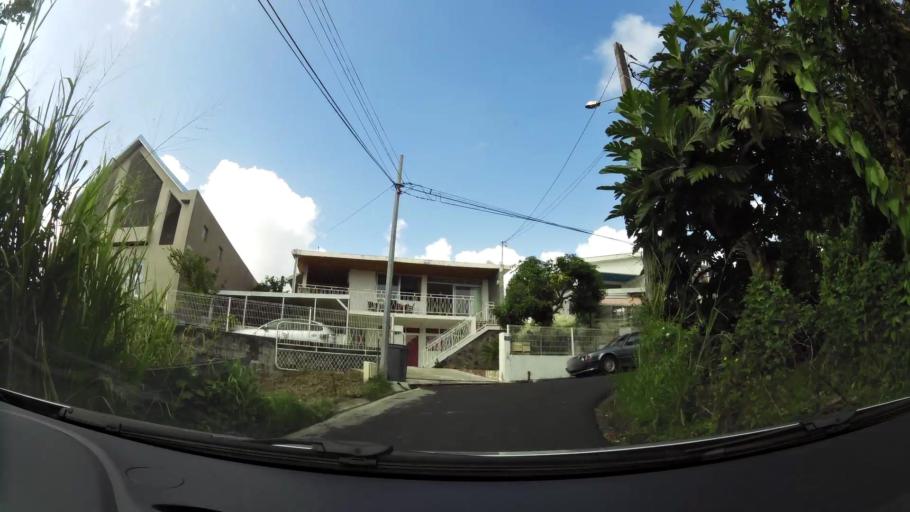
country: MQ
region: Martinique
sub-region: Martinique
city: Fort-de-France
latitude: 14.6242
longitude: -61.0578
